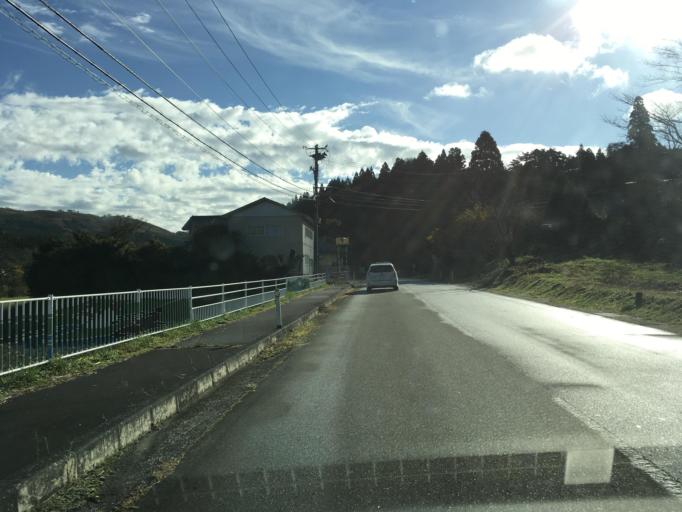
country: JP
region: Iwate
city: Ichinoseki
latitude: 38.8944
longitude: 141.4393
